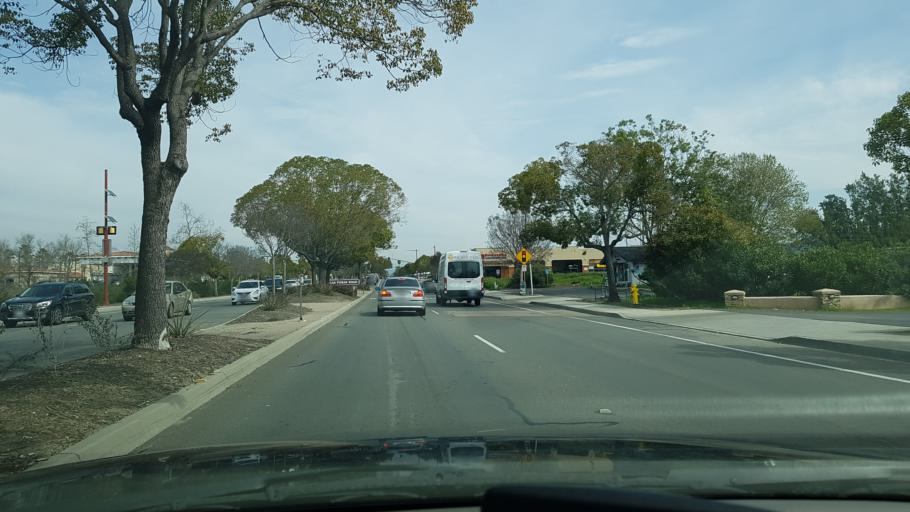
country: US
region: California
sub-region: San Diego County
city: Lake San Marcos
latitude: 33.1325
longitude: -117.1964
